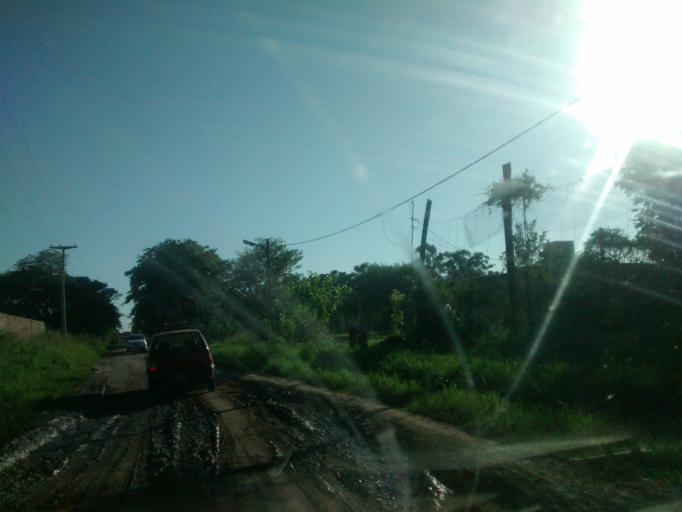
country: AR
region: Chaco
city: Fontana
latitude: -27.4617
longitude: -59.0371
